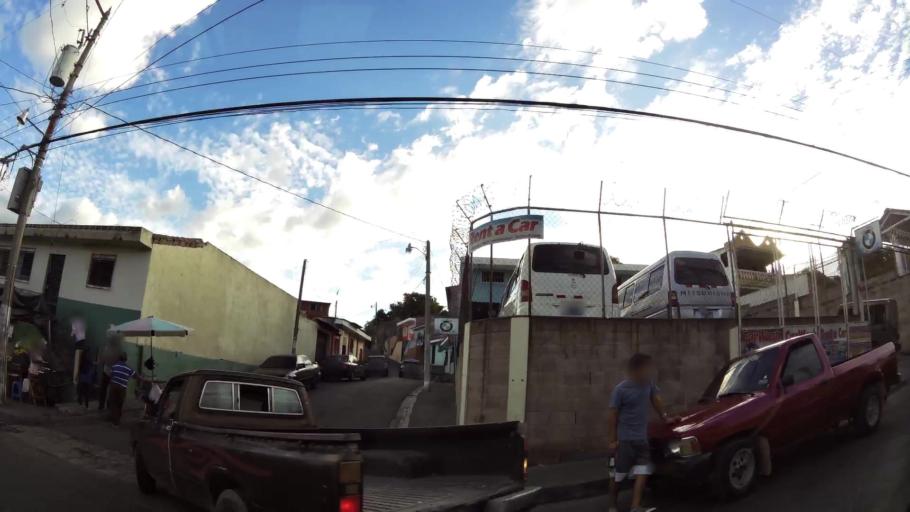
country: SV
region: Cuscatlan
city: Cojutepeque
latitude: 13.7188
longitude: -88.9312
